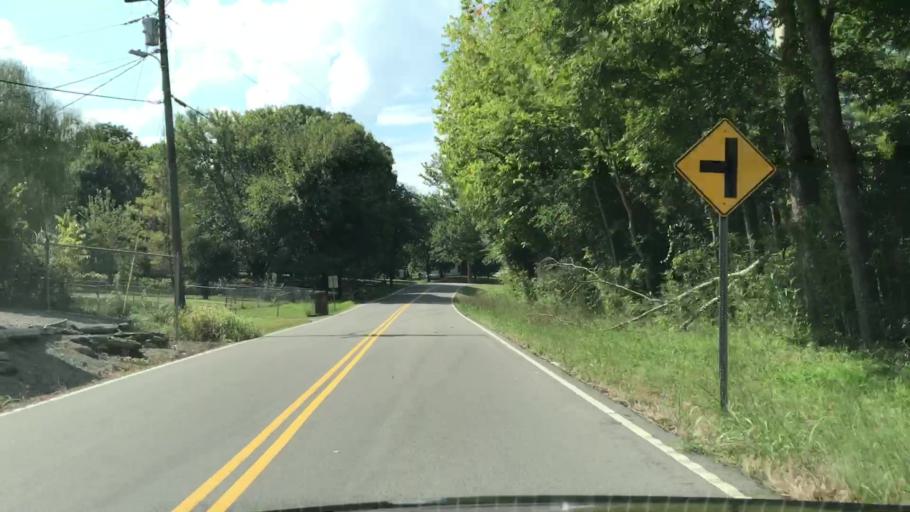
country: US
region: Tennessee
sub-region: Trousdale County
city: Hartsville
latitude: 36.4576
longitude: -86.1766
